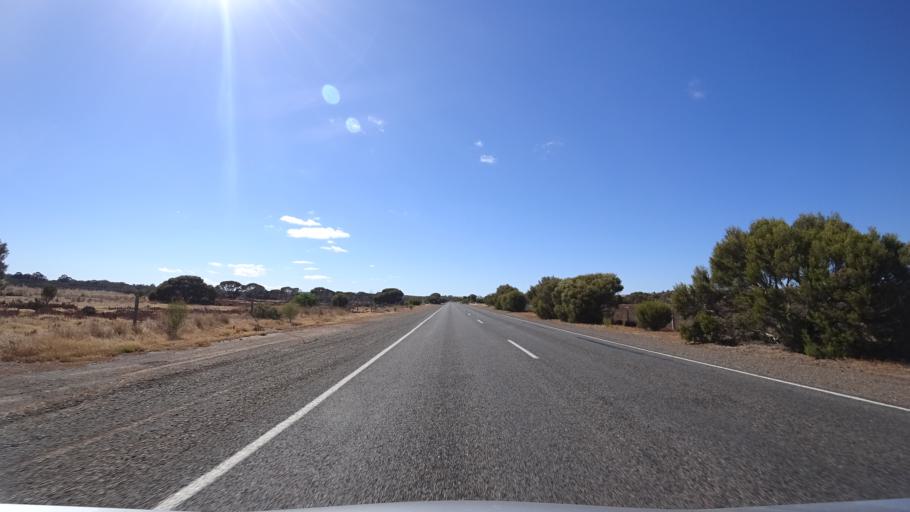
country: AU
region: South Australia
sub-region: Kangaroo Island
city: Kingscote
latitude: -35.7383
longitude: 137.5766
